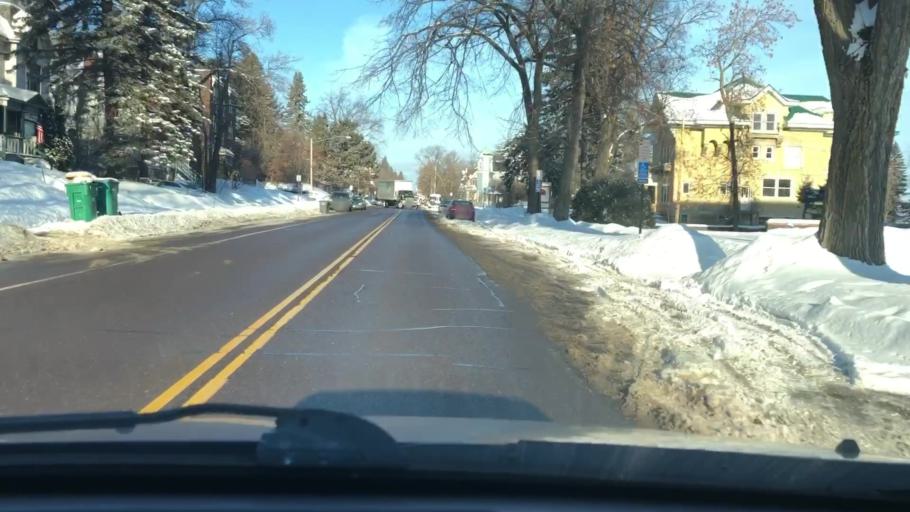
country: US
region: Minnesota
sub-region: Saint Louis County
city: Duluth
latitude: 46.8034
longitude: -92.0767
